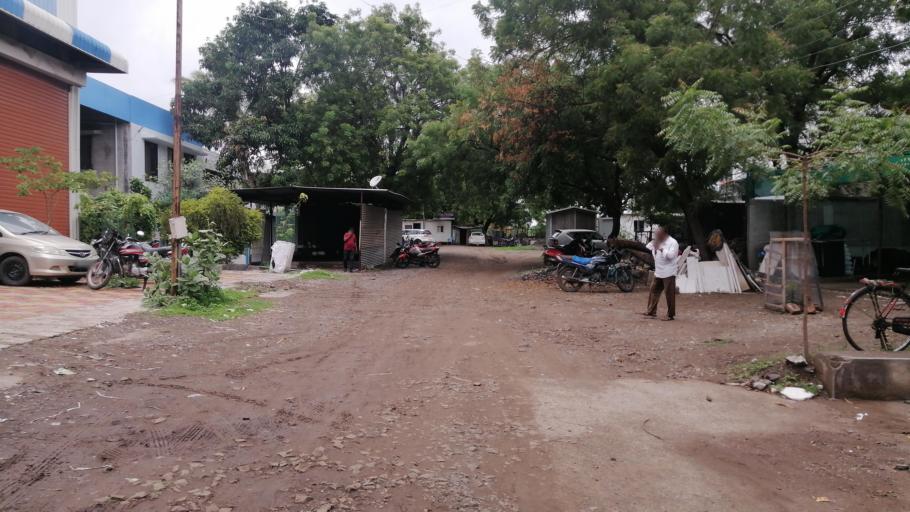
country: IN
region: Maharashtra
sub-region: Aurangabad Division
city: Aurangabad
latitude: 19.8810
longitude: 75.3751
